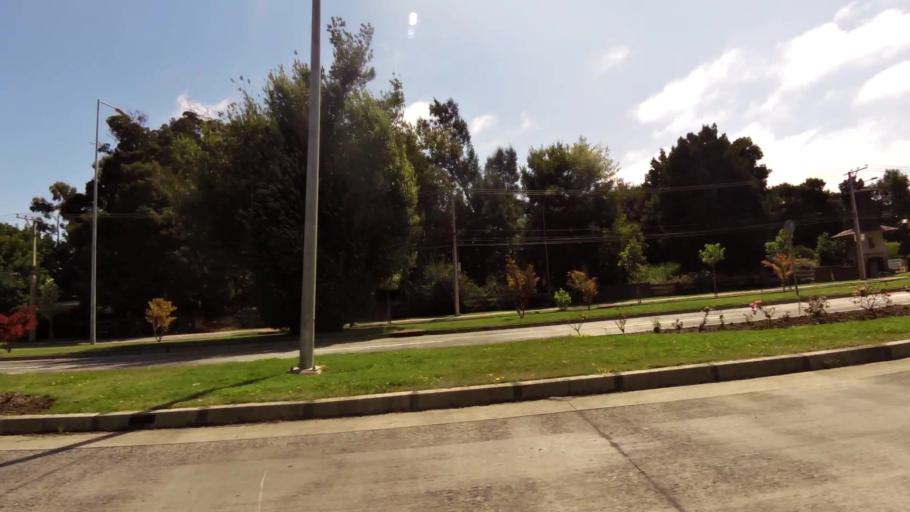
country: CL
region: Biobio
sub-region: Provincia de Concepcion
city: Concepcion
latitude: -36.7859
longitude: -73.0600
